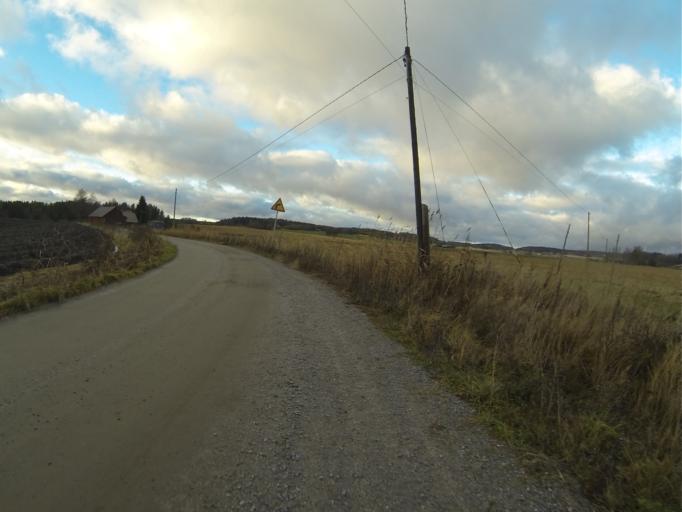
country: FI
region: Varsinais-Suomi
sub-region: Salo
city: Halikko
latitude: 60.4059
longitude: 23.0366
